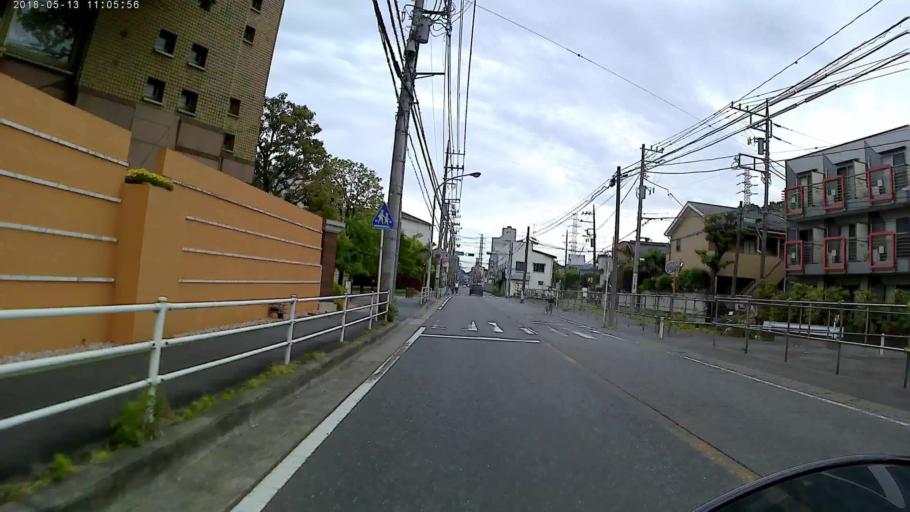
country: JP
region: Tokyo
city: Chofugaoka
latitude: 35.5931
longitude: 139.6149
